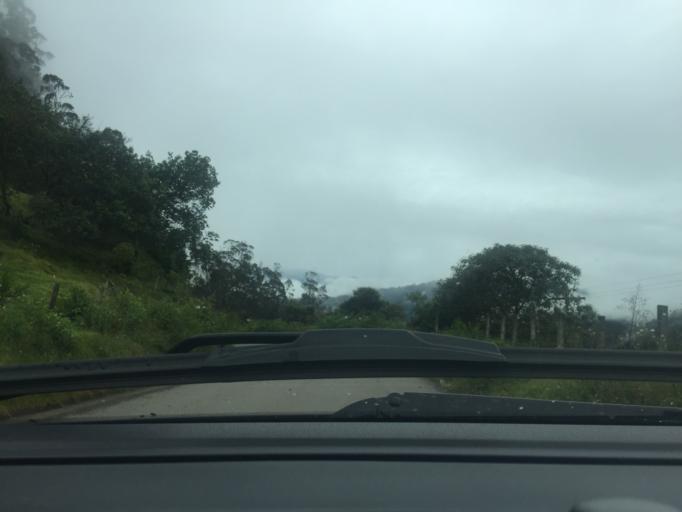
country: CO
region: Cundinamarca
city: Junin
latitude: 4.8113
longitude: -73.7316
